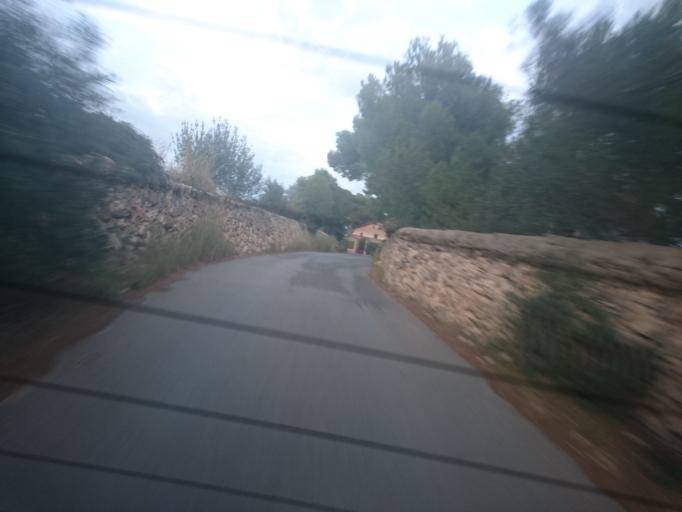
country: ES
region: Catalonia
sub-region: Provincia de Barcelona
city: Vilanova i la Geltru
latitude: 41.2109
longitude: 1.7108
